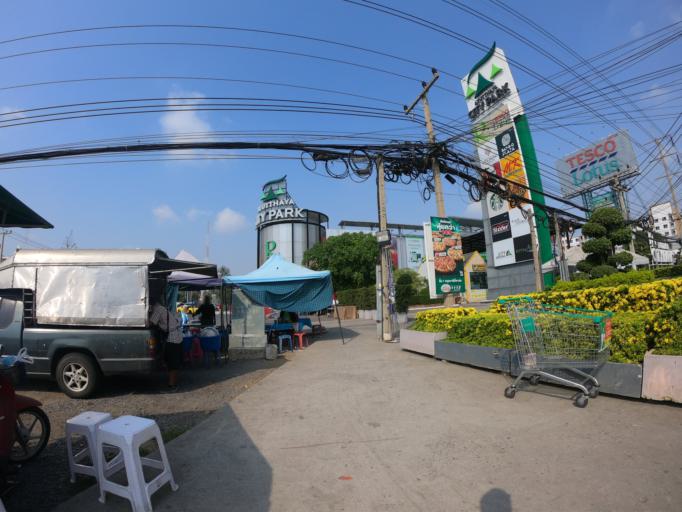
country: TH
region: Phra Nakhon Si Ayutthaya
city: Phra Nakhon Si Ayutthaya
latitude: 14.3379
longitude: 100.6187
